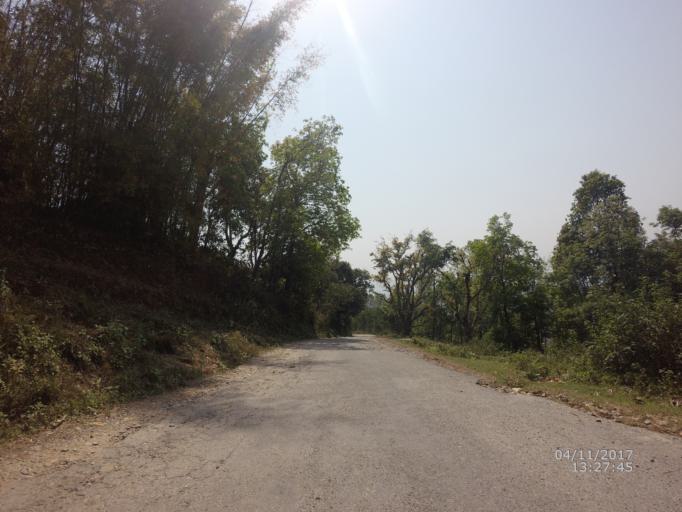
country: NP
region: Western Region
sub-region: Gandaki Zone
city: Pokhara
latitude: 28.1996
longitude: 84.0414
